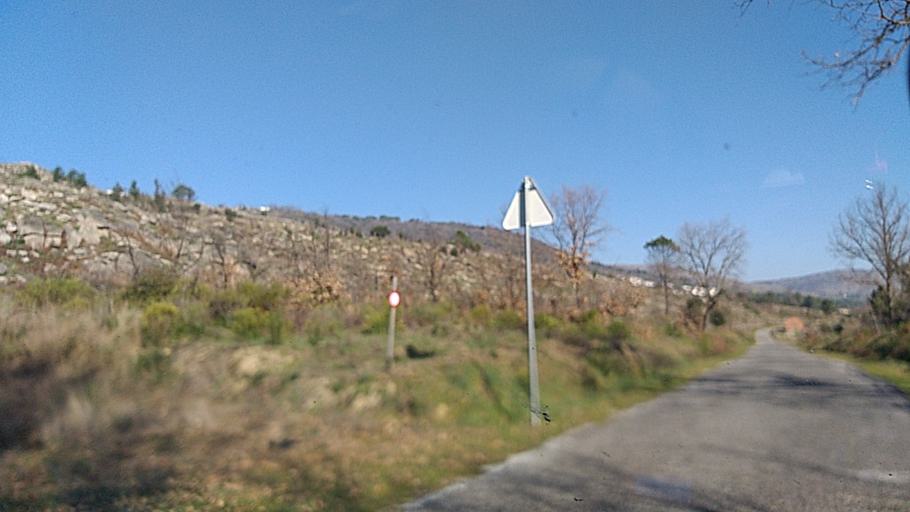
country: PT
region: Guarda
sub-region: Celorico da Beira
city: Celorico da Beira
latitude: 40.6717
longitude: -7.4567
